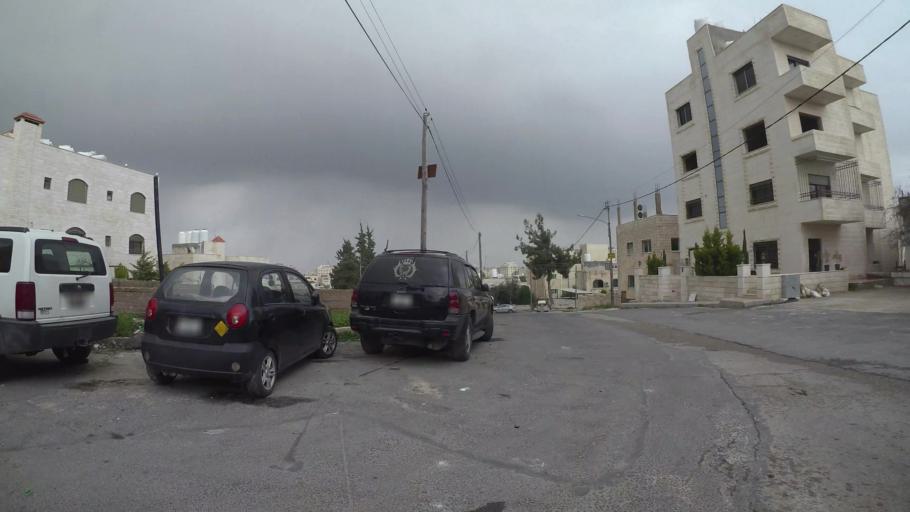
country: JO
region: Amman
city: Umm as Summaq
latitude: 31.8871
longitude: 35.8541
